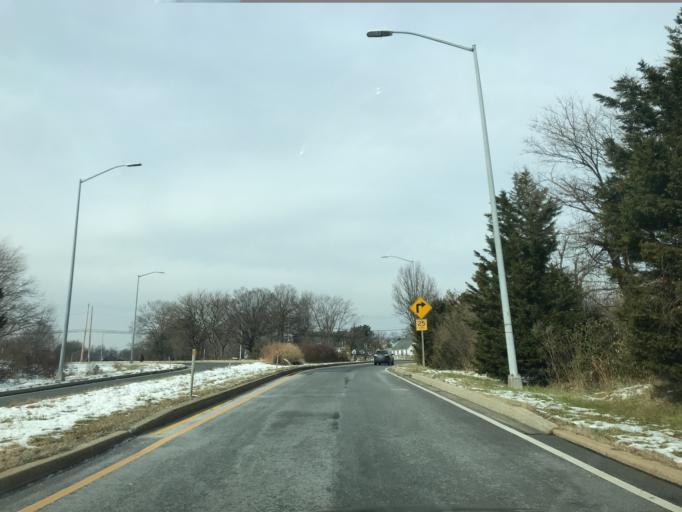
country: US
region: Maryland
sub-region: Baltimore County
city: Overlea
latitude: 39.3696
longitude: -76.5115
